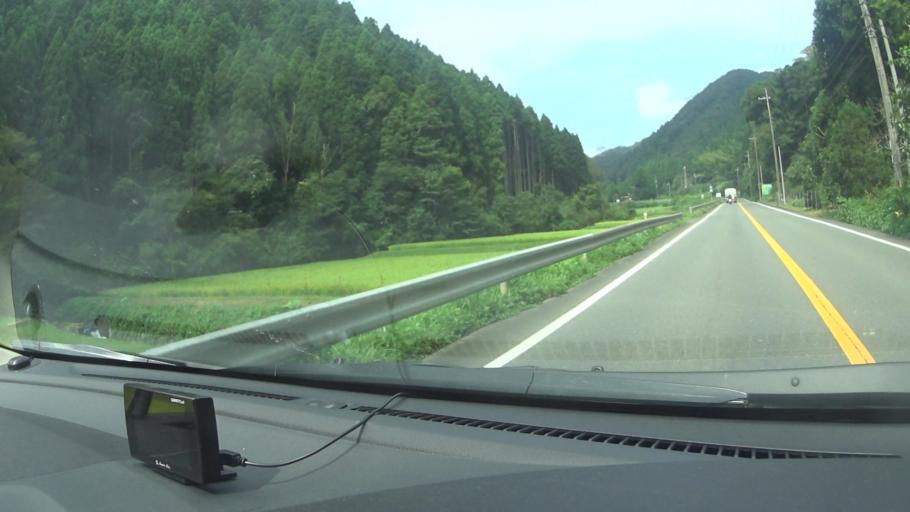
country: JP
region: Kyoto
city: Ayabe
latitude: 35.2349
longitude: 135.3306
